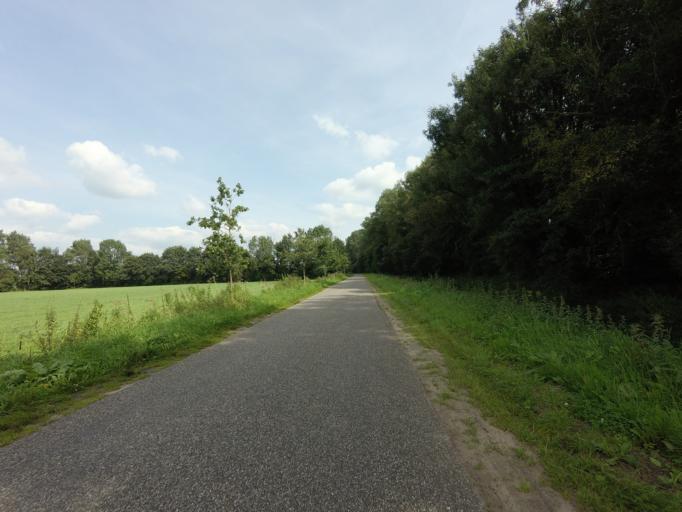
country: DE
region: Lower Saxony
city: Lage
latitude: 52.3966
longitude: 6.9258
